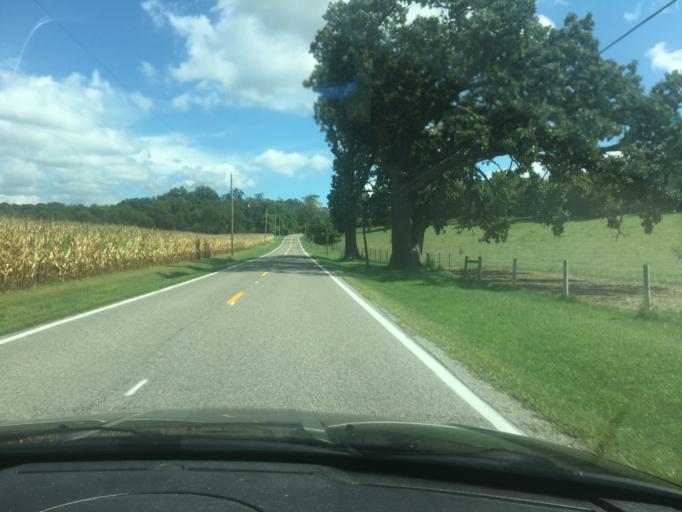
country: US
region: Ohio
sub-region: Logan County
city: West Liberty
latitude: 40.2346
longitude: -83.7267
